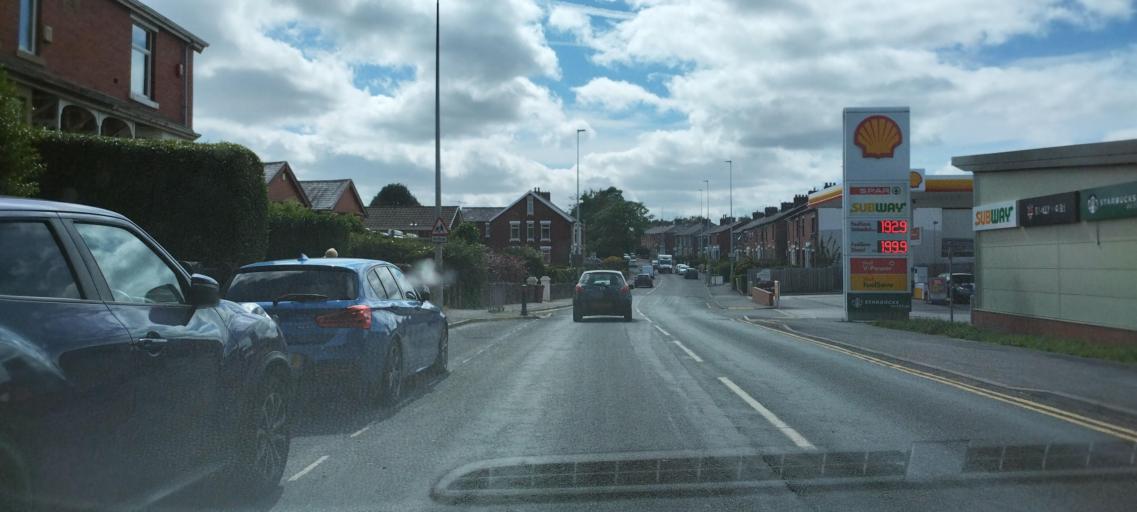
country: GB
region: England
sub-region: Blackburn with Darwen
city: Blackburn
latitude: 53.7275
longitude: -2.5346
